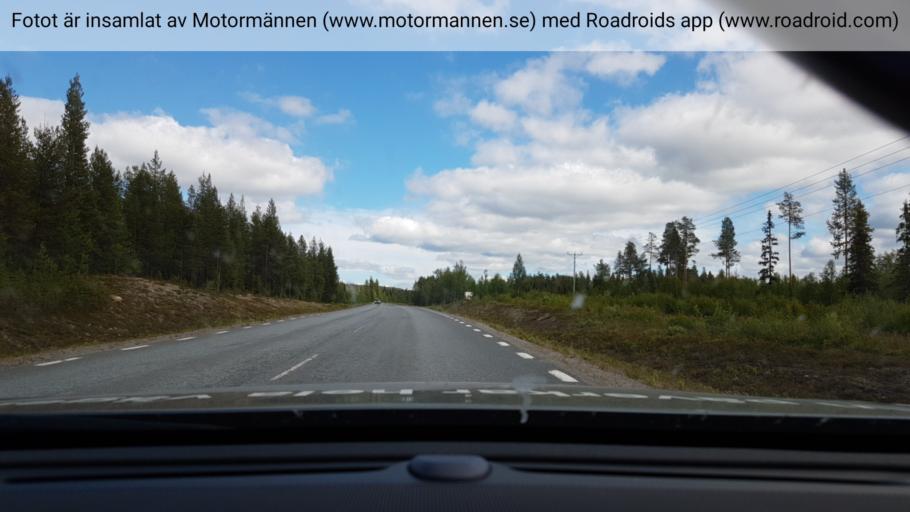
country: SE
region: Vaesterbotten
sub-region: Sorsele Kommun
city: Sorsele
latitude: 65.5372
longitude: 17.5842
